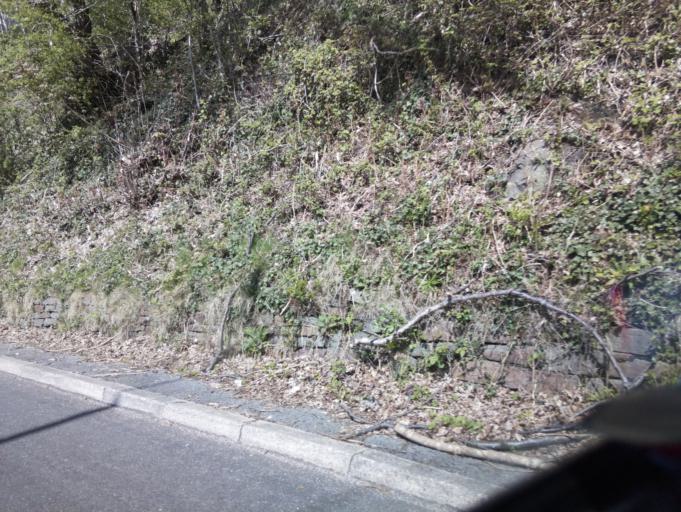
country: GB
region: Wales
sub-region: Rhondda Cynon Taf
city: Pontypridd
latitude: 51.6021
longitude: -3.3298
